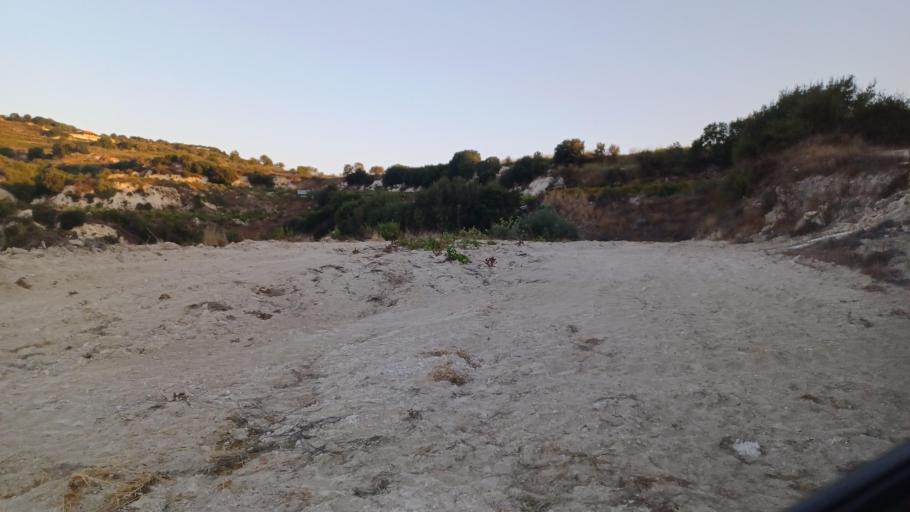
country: CY
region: Pafos
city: Mesogi
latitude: 34.8543
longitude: 32.5031
